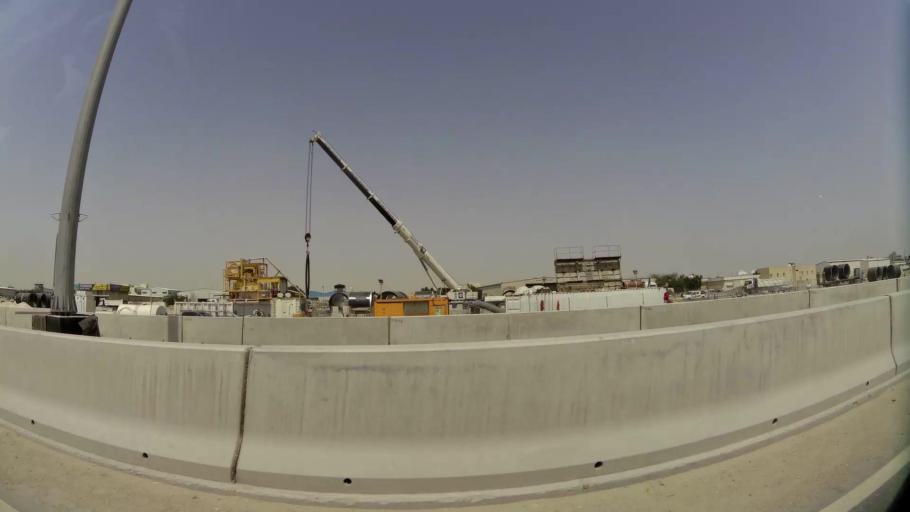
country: QA
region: Al Wakrah
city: Al Wukayr
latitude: 25.1898
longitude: 51.4489
